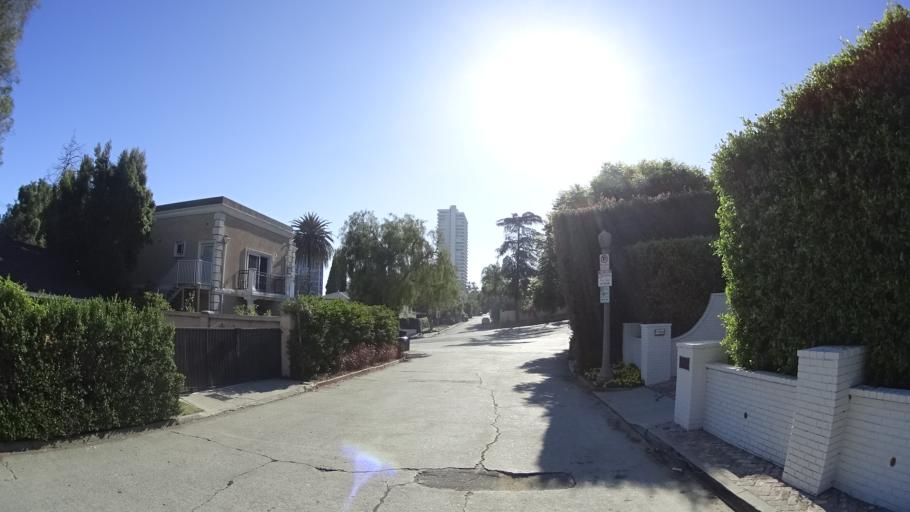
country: US
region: California
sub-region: Los Angeles County
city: Beverly Hills
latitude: 34.0914
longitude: -118.3892
